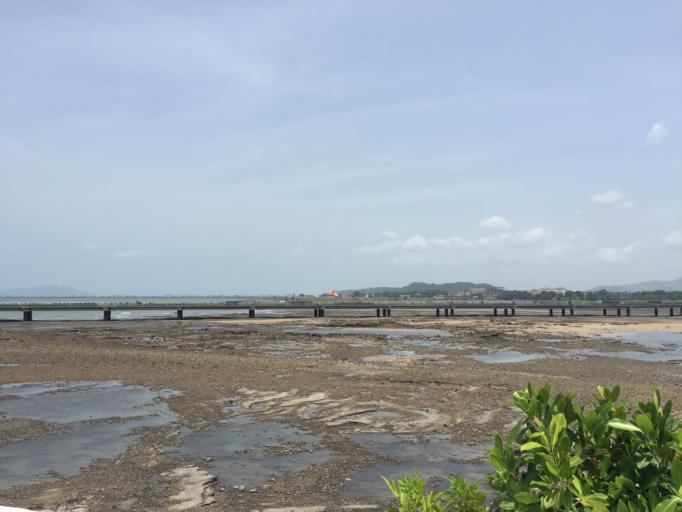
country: PA
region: Panama
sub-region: Distrito de Panama
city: Ancon
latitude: 8.9493
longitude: -79.5322
